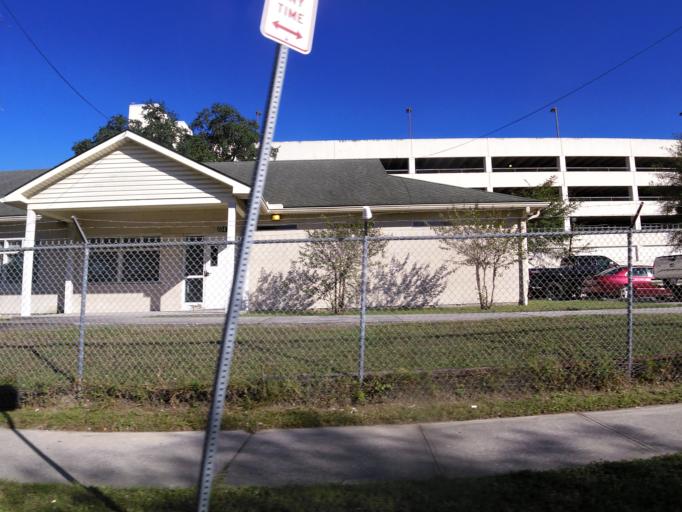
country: US
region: Florida
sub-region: Duval County
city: Jacksonville
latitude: 30.3497
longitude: -81.6662
